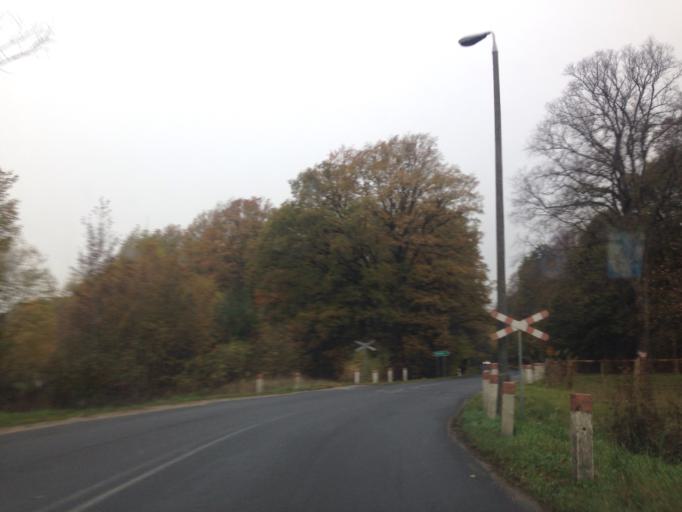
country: PL
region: Kujawsko-Pomorskie
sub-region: Powiat brodnicki
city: Bobrowo
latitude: 53.2648
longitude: 19.3290
